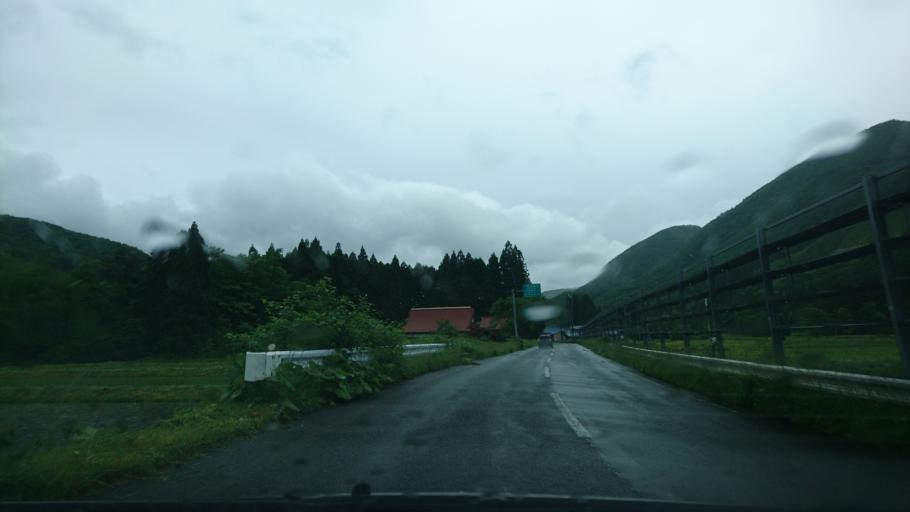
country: JP
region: Iwate
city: Ichinoseki
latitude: 38.9964
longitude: 140.8996
